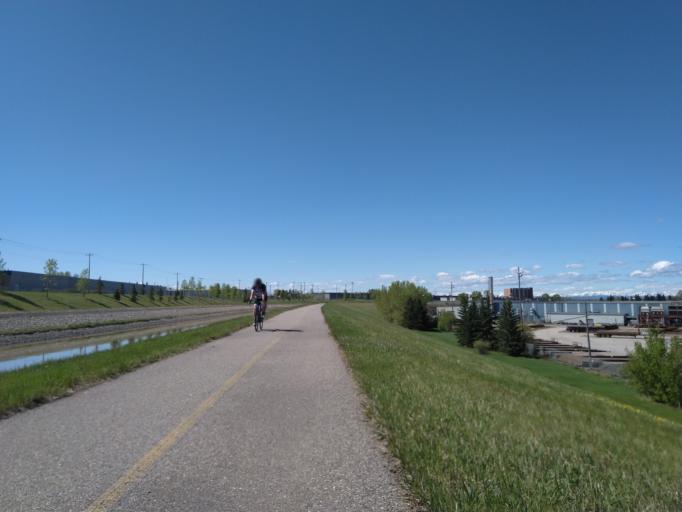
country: CA
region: Alberta
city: Calgary
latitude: 50.9872
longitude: -113.9883
